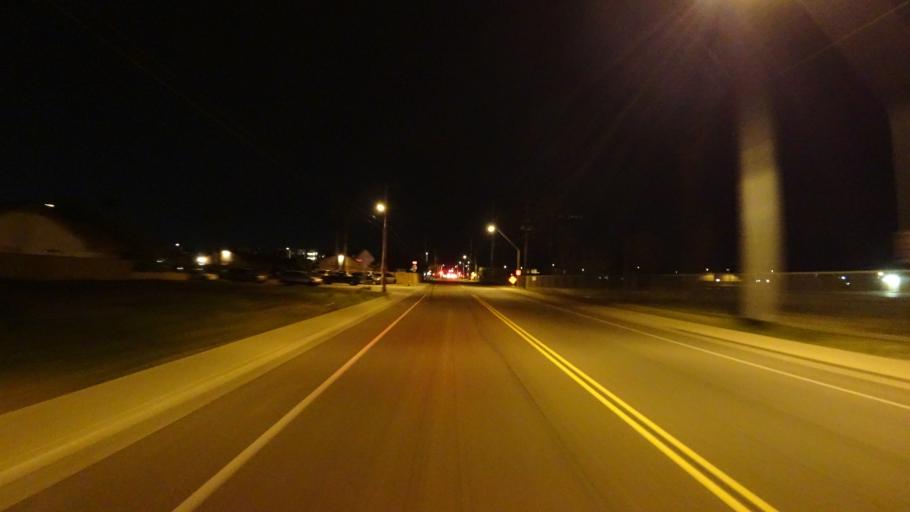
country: US
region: Arizona
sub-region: Maricopa County
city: Mesa
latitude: 33.4121
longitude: -111.8141
